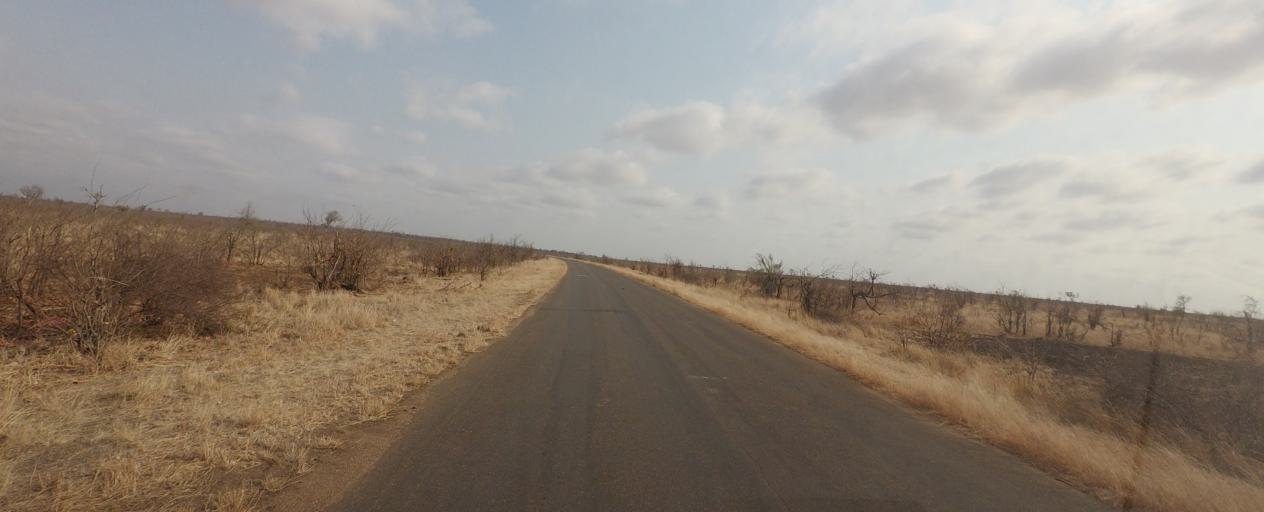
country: ZA
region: Limpopo
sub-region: Vhembe District Municipality
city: Mutale
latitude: -22.9007
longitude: 31.2529
